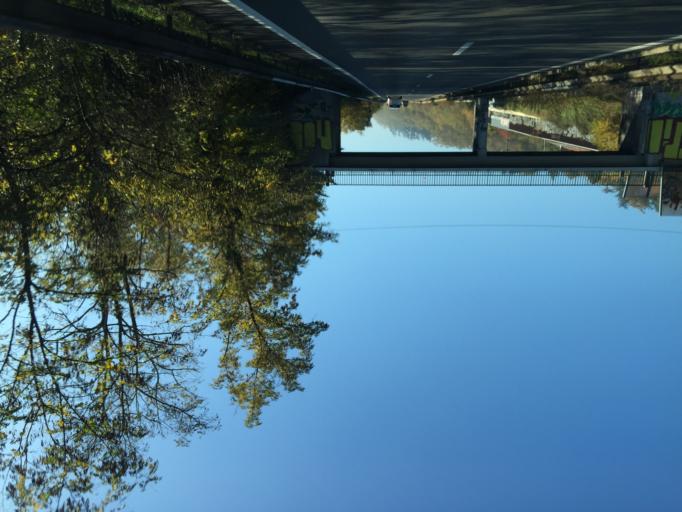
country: FR
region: Rhone-Alpes
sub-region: Departement de la Loire
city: Rive-de-Gier
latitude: 45.5238
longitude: 4.5980
